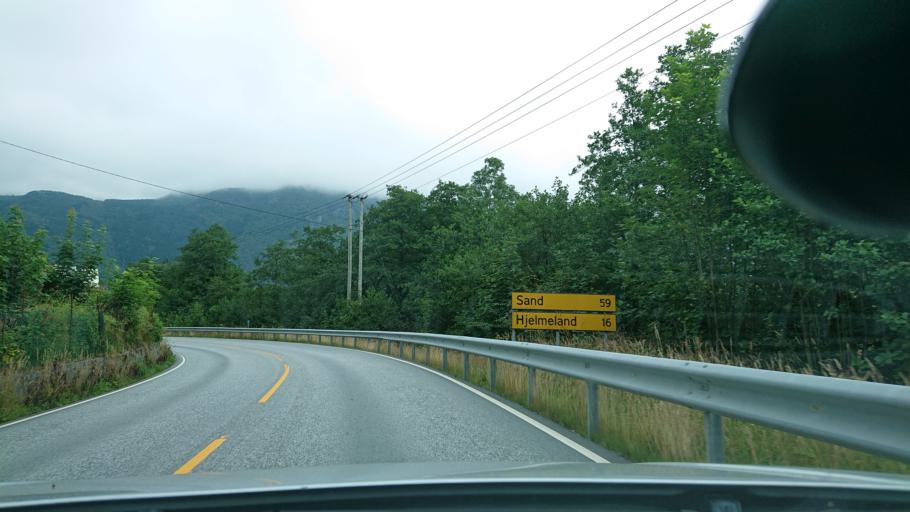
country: NO
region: Rogaland
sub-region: Hjelmeland
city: Hjelmelandsvagen
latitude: 59.1536
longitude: 6.1729
